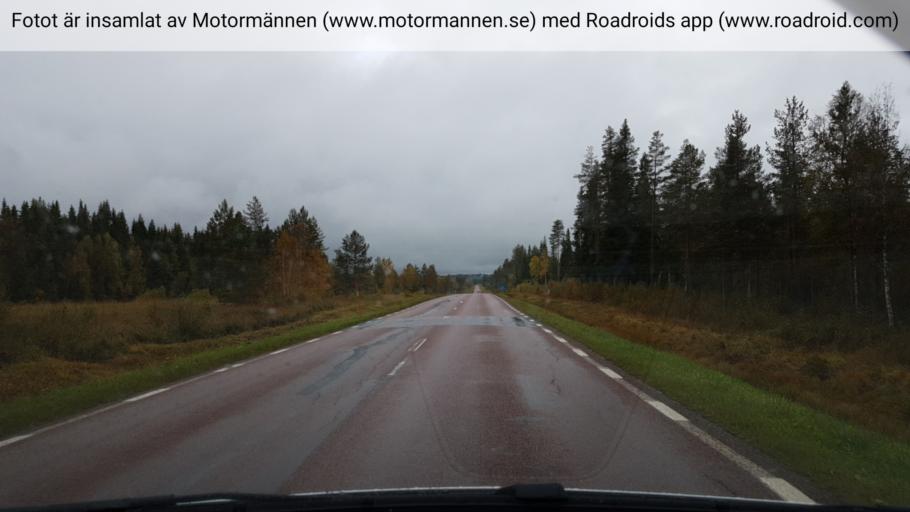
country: SE
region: Jaemtland
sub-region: Stroemsunds Kommun
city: Stroemsund
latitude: 63.7652
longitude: 15.5023
